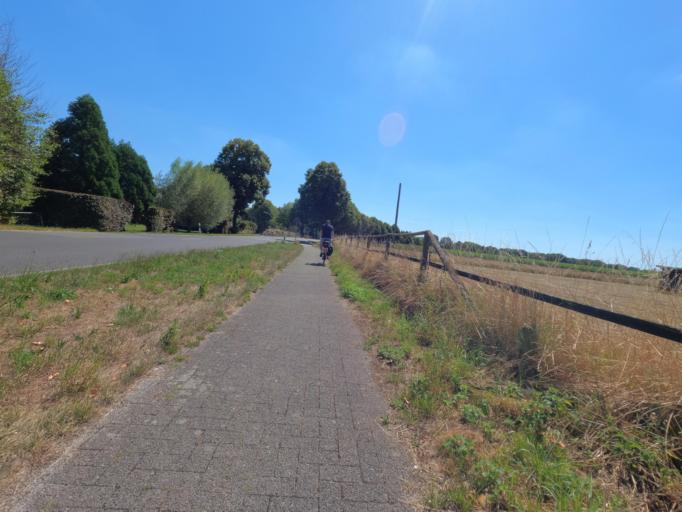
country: DE
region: North Rhine-Westphalia
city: Wegberg
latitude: 51.1523
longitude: 6.2708
